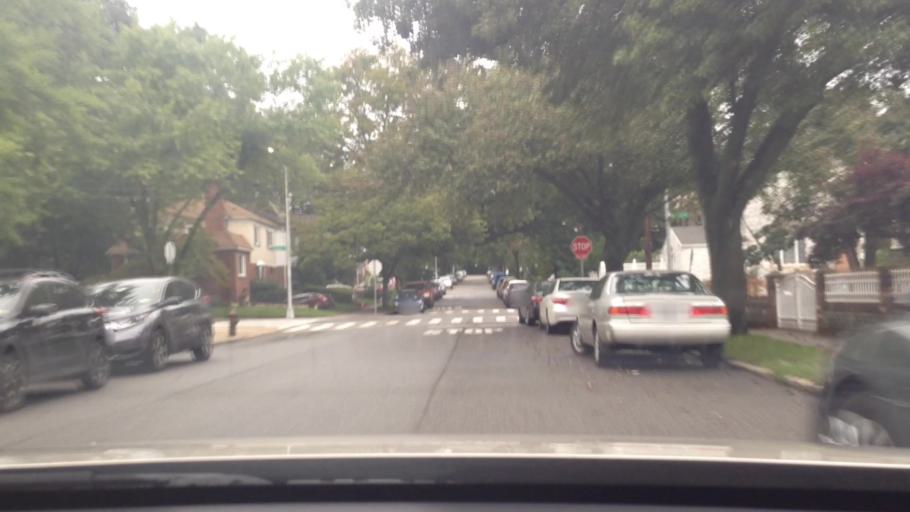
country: US
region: New York
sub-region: Nassau County
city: Bellerose Terrace
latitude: 40.7349
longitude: -73.7386
